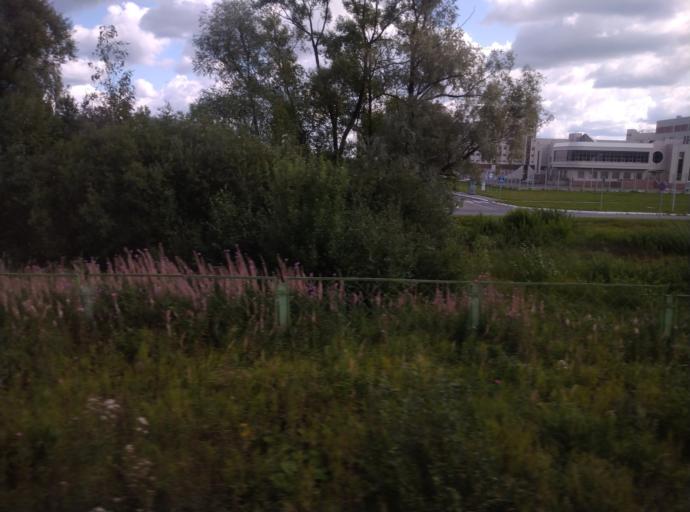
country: RU
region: St.-Petersburg
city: Kolpino
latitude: 59.7394
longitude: 30.6270
